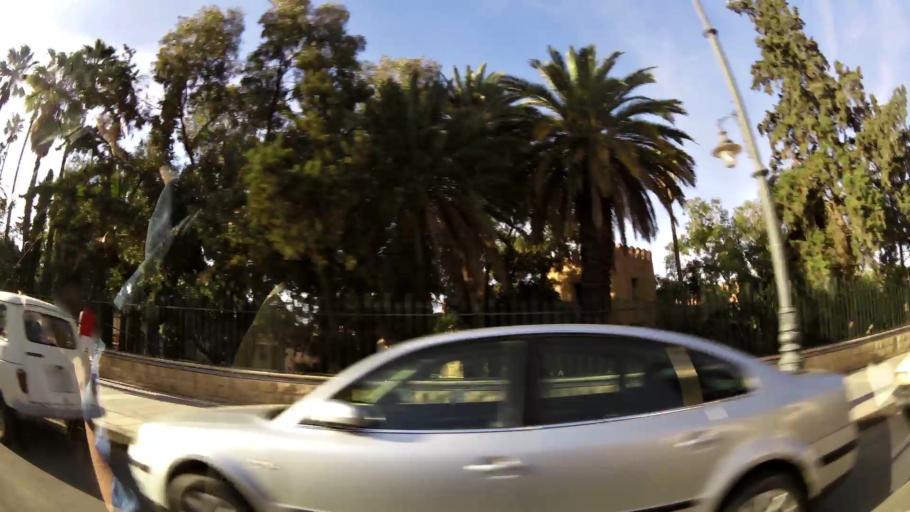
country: MA
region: Oriental
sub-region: Oujda-Angad
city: Oujda
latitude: 34.6770
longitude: -1.9144
